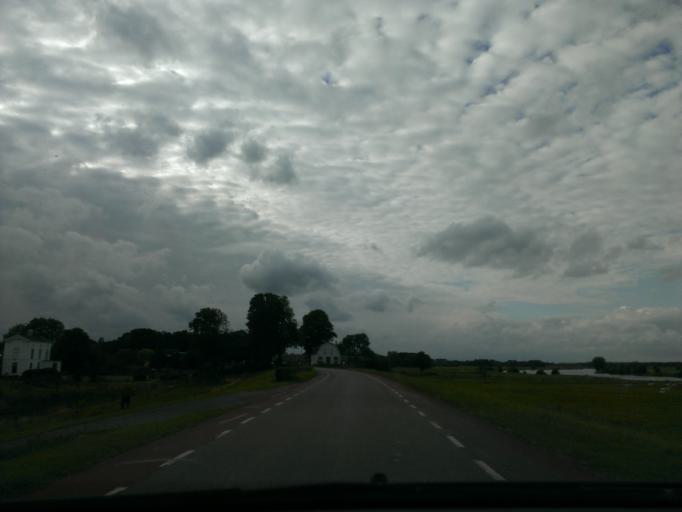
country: NL
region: Gelderland
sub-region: Gemeente Voorst
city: Twello
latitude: 52.2744
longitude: 6.1129
